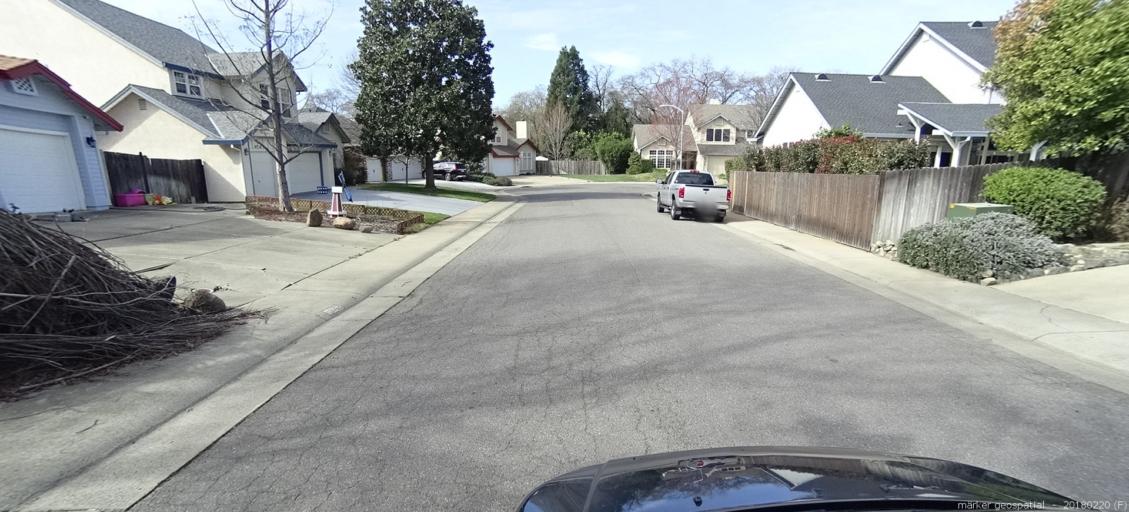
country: US
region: California
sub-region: Sacramento County
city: Orangevale
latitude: 38.6745
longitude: -121.2317
